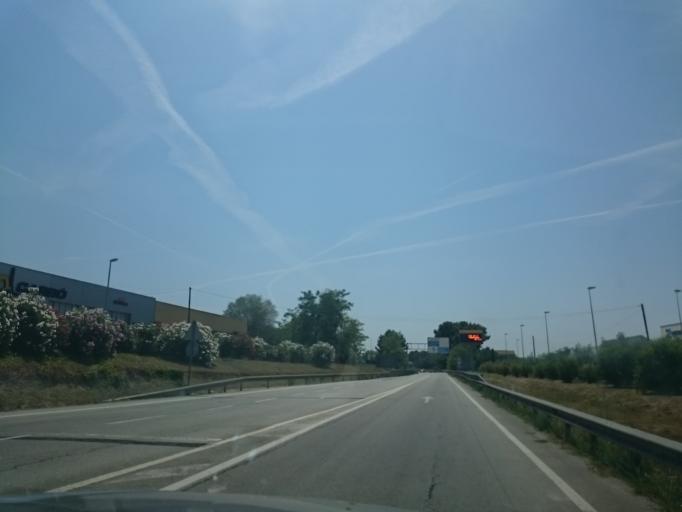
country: ES
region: Catalonia
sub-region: Provincia de Barcelona
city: Vilafranca del Penedes
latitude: 41.3316
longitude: 1.6794
